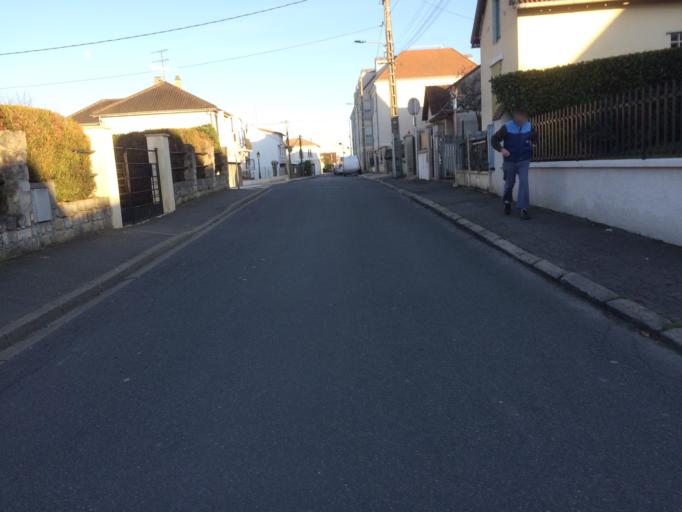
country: FR
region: Ile-de-France
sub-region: Departement de l'Essonne
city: Igny
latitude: 48.7332
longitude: 2.2196
